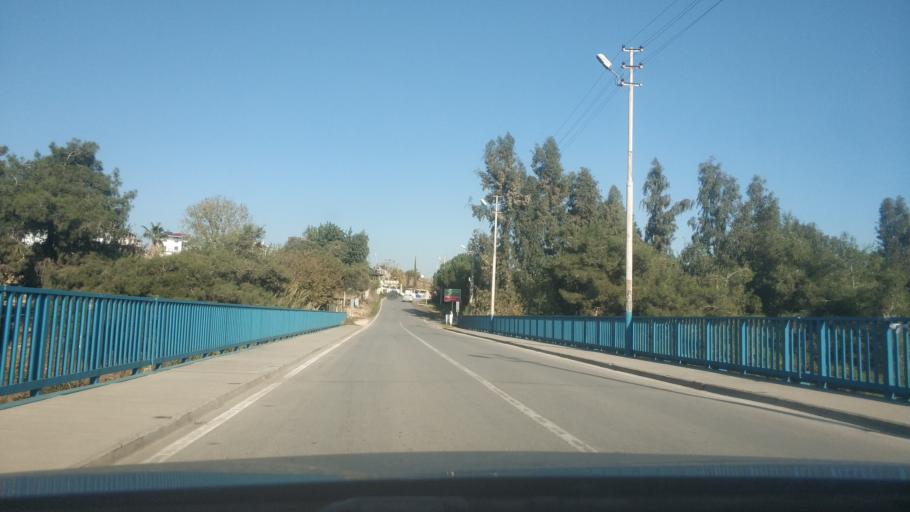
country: TR
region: Adana
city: Adana
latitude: 37.1048
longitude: 35.2954
